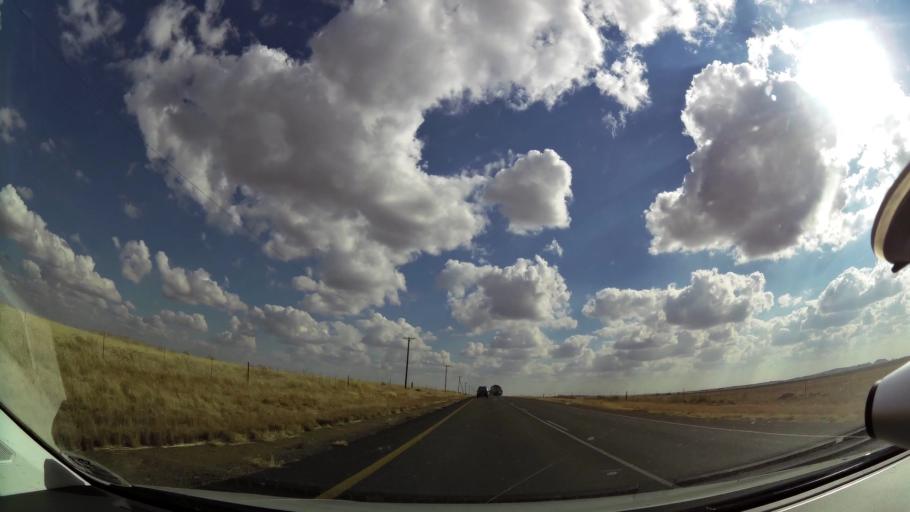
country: ZA
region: Orange Free State
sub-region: Xhariep District Municipality
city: Koffiefontein
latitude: -29.1328
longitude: 25.5452
